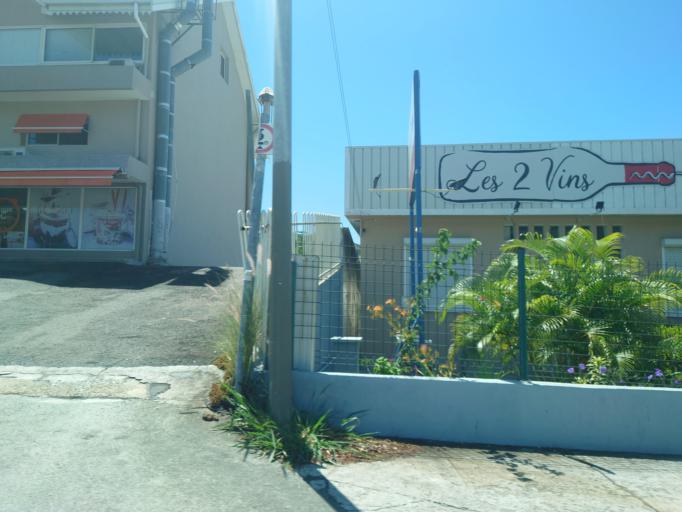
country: NC
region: South Province
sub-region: Noumea
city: Noumea
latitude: -22.2682
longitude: 166.4557
